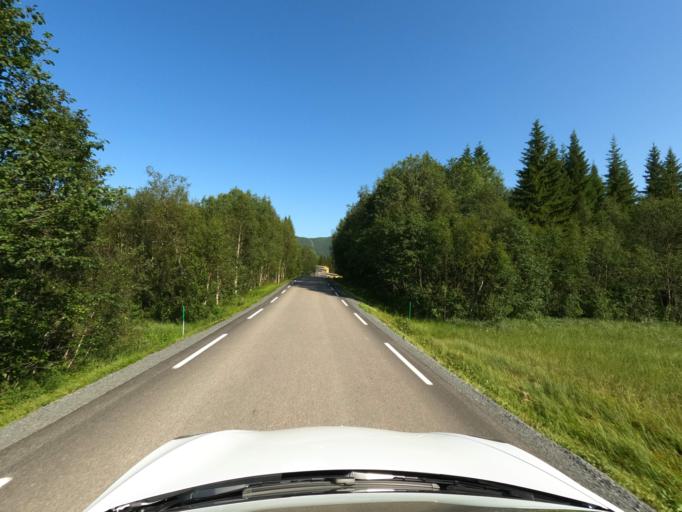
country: NO
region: Nordland
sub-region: Narvik
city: Narvik
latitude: 68.3933
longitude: 17.3189
